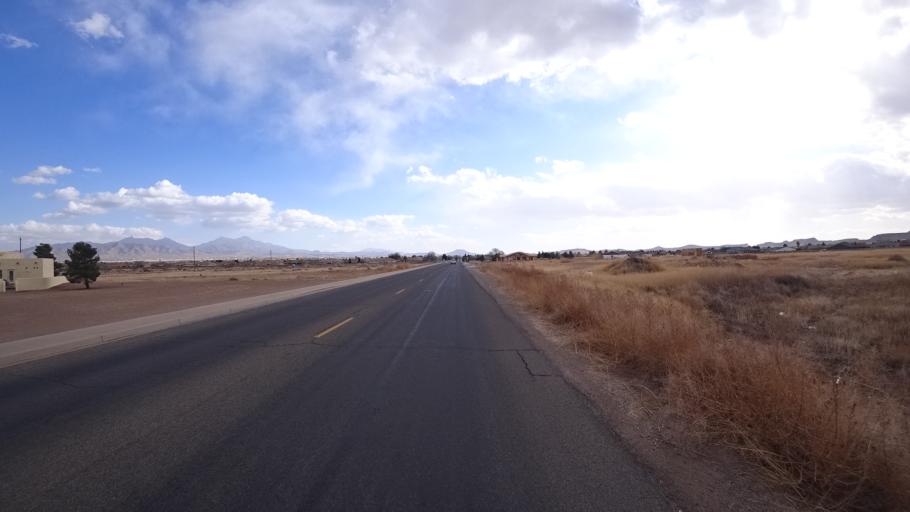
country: US
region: Arizona
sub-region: Mohave County
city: New Kingman-Butler
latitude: 35.2381
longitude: -114.0248
